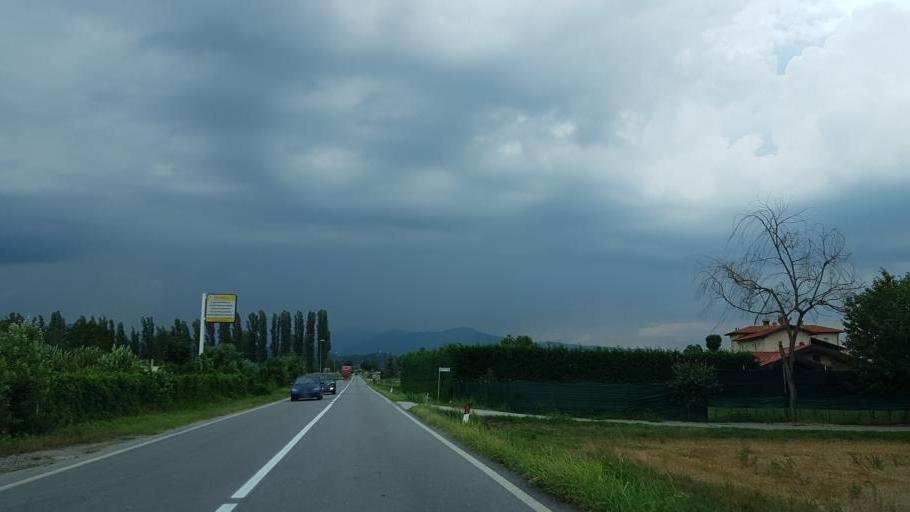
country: IT
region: Piedmont
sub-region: Provincia di Cuneo
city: San Rocco
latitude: 44.3944
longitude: 7.4556
